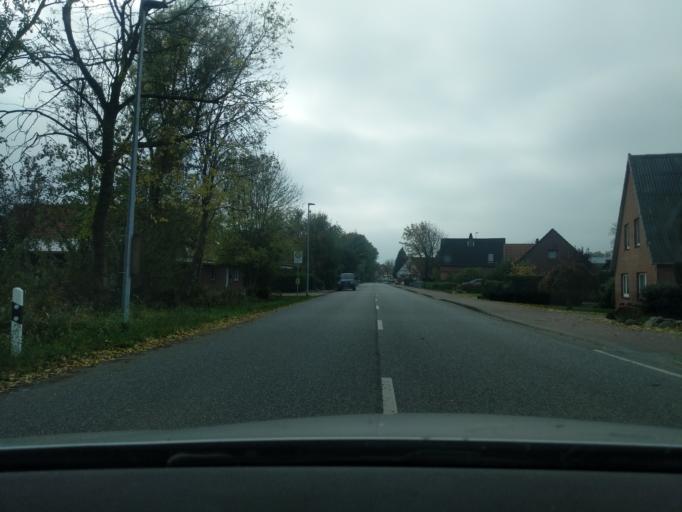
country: DE
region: Lower Saxony
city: Otterndorf
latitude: 53.8120
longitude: 8.9166
